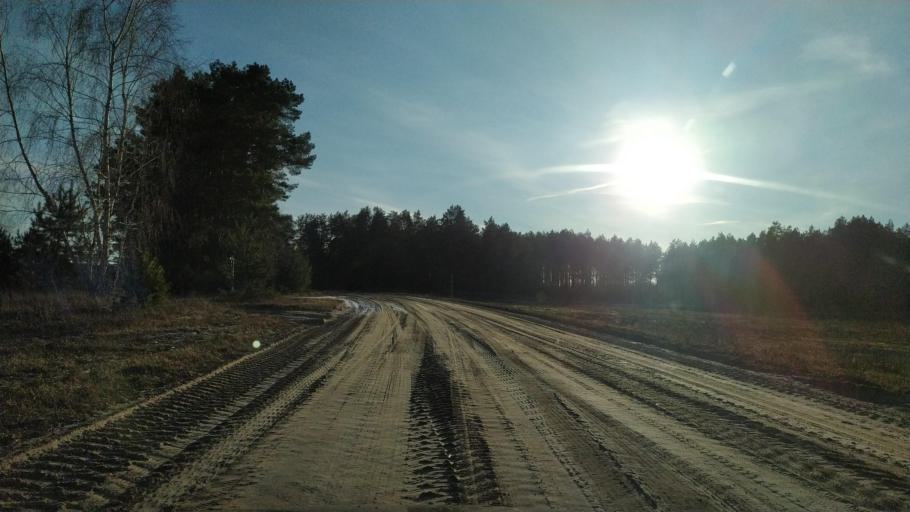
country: BY
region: Brest
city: Pruzhany
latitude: 52.5500
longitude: 24.2867
